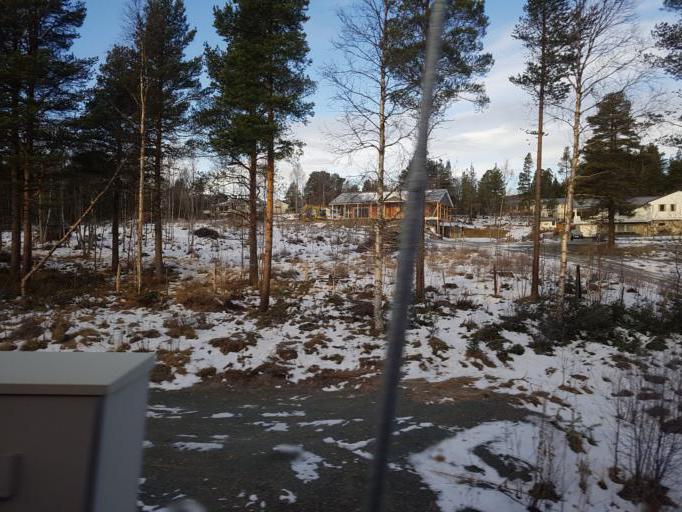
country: NO
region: Sor-Trondelag
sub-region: Oppdal
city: Oppdal
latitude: 62.6569
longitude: 9.8807
